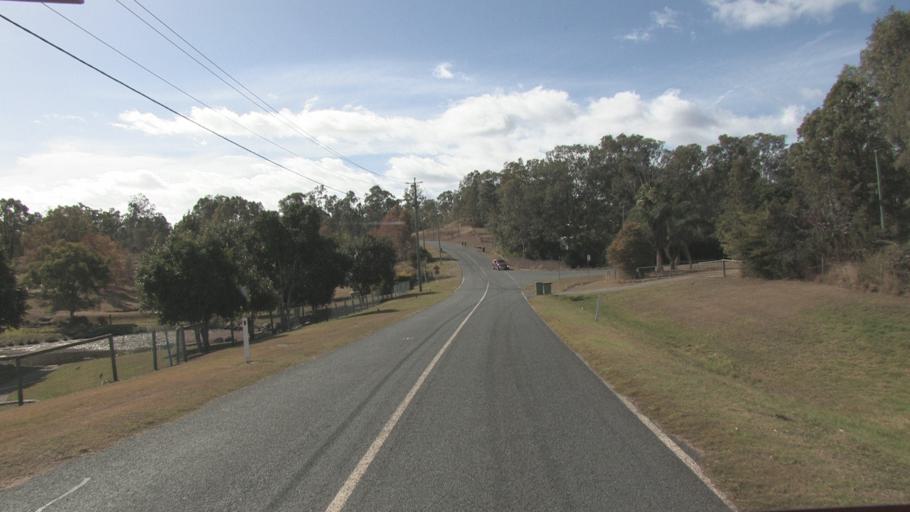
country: AU
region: Queensland
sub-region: Logan
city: Cedar Vale
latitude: -27.8892
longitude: 152.9940
